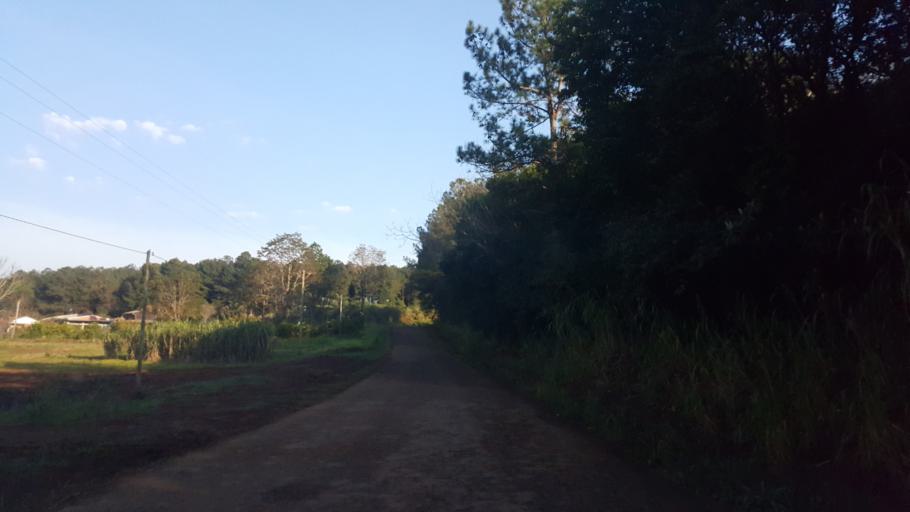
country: AR
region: Misiones
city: Capiovi
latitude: -26.8899
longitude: -55.0575
